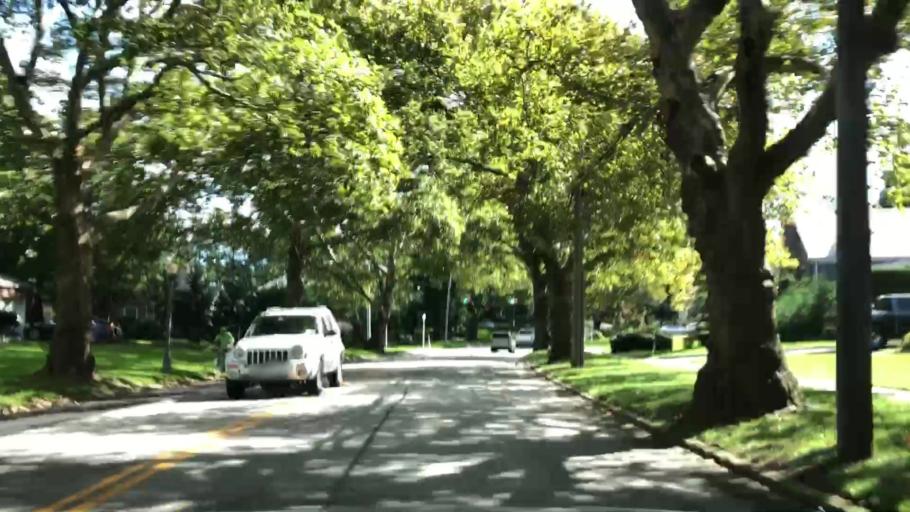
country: US
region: New York
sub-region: Nassau County
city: Munsey Park
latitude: 40.8007
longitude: -73.6778
